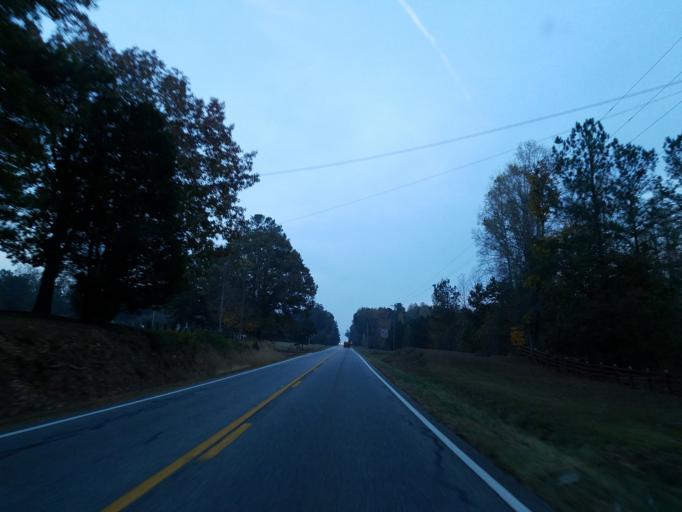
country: US
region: Georgia
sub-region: Pickens County
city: Jasper
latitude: 34.5466
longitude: -84.5875
